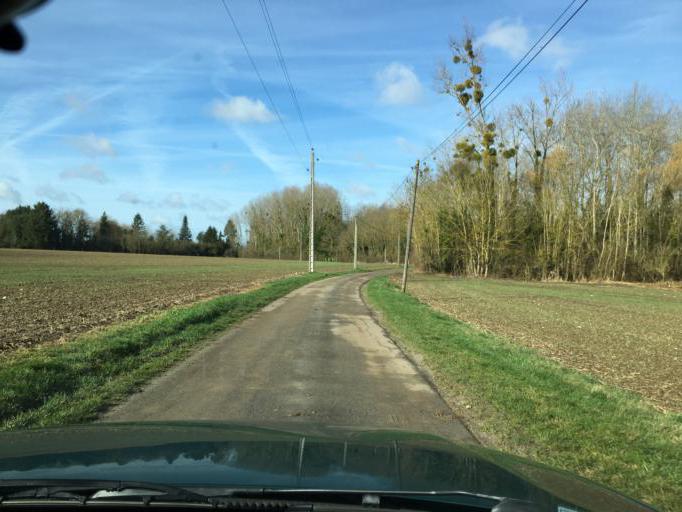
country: FR
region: Centre
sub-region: Departement du Loiret
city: Meung-sur-Loire
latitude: 47.8575
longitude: 1.6888
